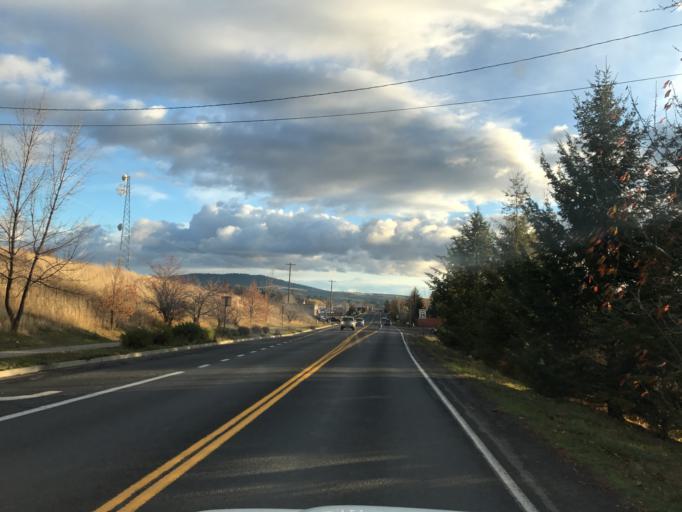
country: US
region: Idaho
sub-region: Latah County
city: Moscow
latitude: 46.7465
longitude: -117.0016
